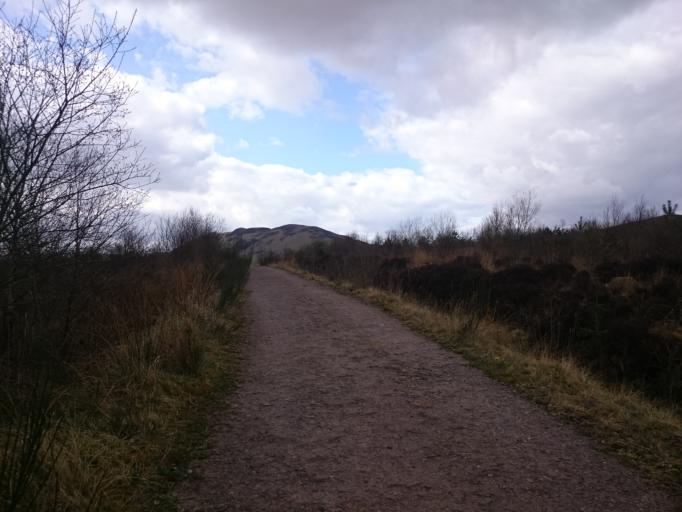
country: GB
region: Scotland
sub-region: Stirling
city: Killearn
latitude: 56.0917
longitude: -4.4846
